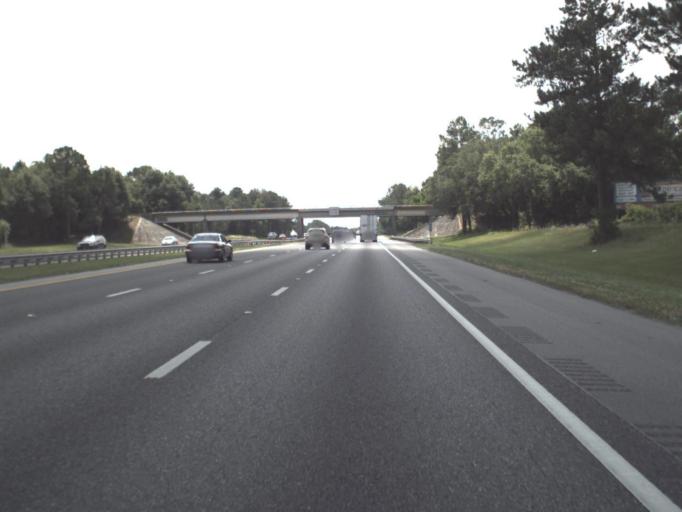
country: US
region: Florida
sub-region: Suwannee County
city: Wellborn
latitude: 30.2921
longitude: -82.7786
